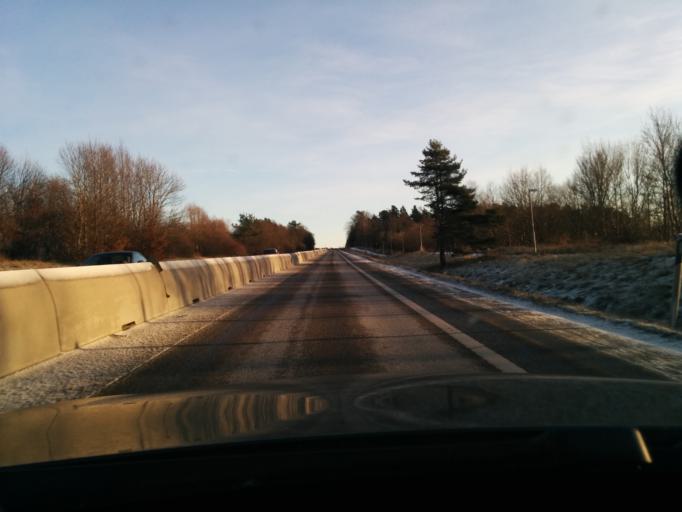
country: SE
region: Stockholm
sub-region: Upplands Vasby Kommun
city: Upplands Vaesby
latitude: 59.4740
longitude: 17.8932
